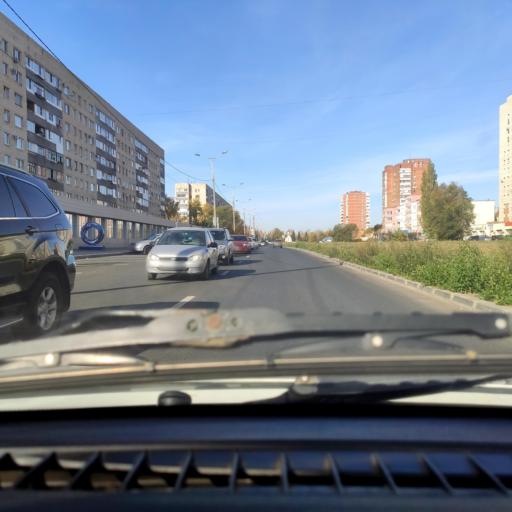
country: RU
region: Samara
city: Tol'yatti
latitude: 53.5017
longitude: 49.4211
